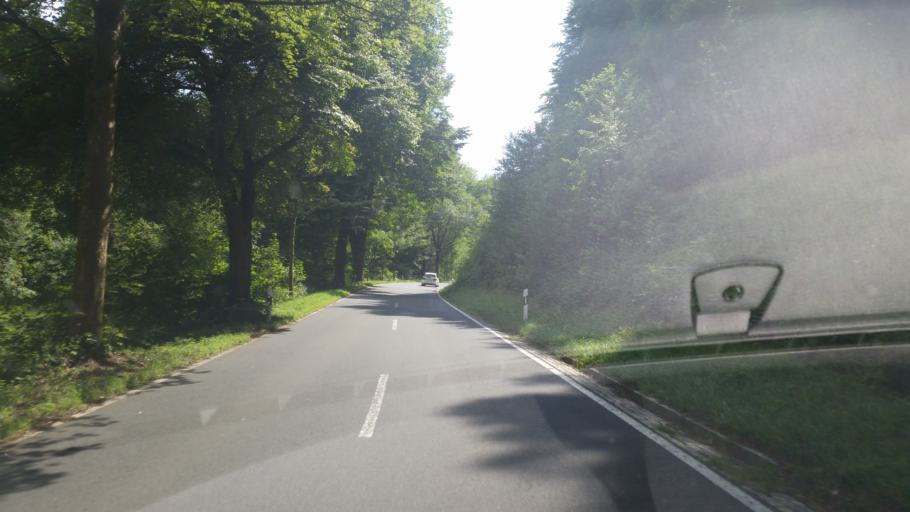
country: DE
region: Saxony
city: Glashutte
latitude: 50.8404
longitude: 13.7313
